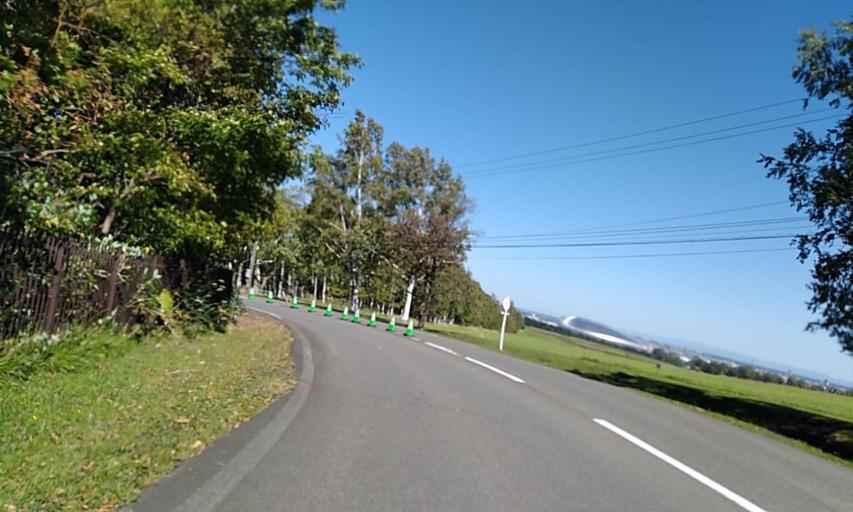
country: JP
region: Hokkaido
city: Sapporo
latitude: 43.0021
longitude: 141.3935
